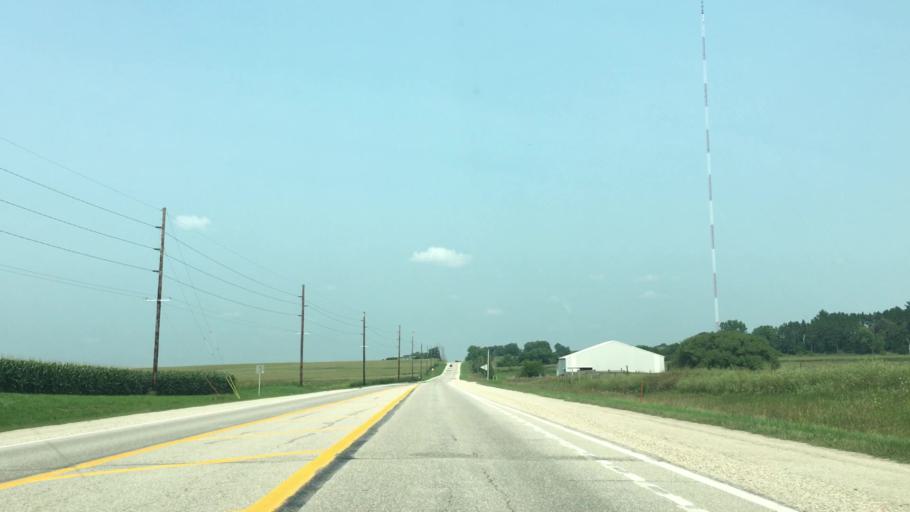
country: US
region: Iowa
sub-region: Benton County
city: Urbana
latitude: 42.2864
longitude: -91.8900
